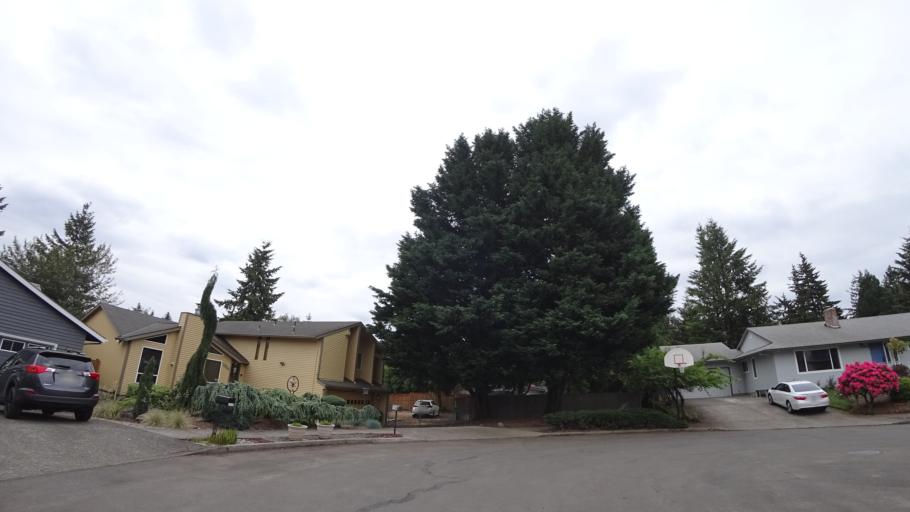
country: US
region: Oregon
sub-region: Multnomah County
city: Lents
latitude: 45.5108
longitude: -122.5454
